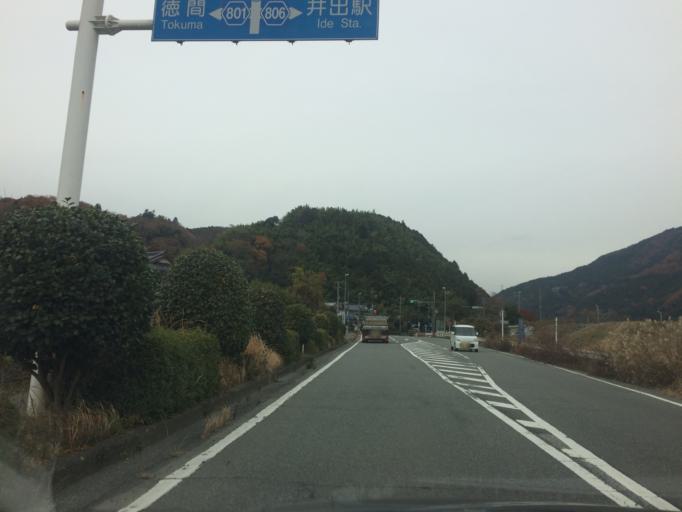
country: JP
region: Shizuoka
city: Fujinomiya
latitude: 35.2507
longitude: 138.4798
